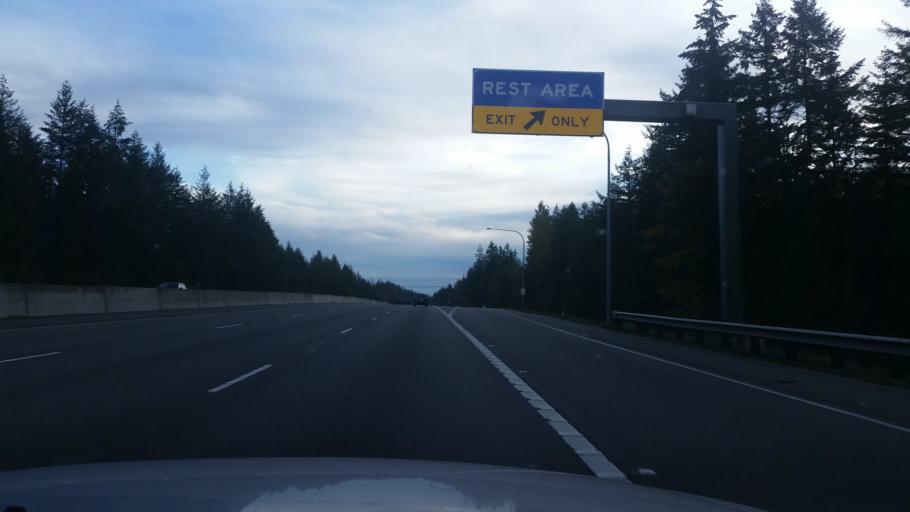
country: US
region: Washington
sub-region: Thurston County
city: Grand Mound
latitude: 46.8750
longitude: -122.9680
